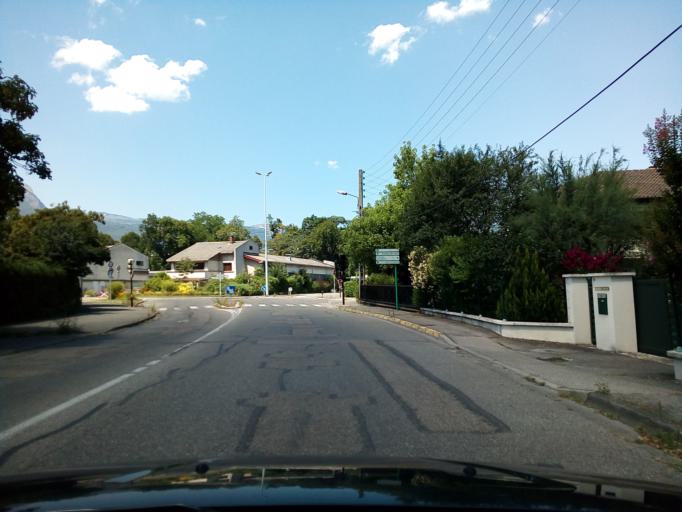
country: FR
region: Rhone-Alpes
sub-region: Departement de l'Isere
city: Echirolles
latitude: 45.1429
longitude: 5.7294
